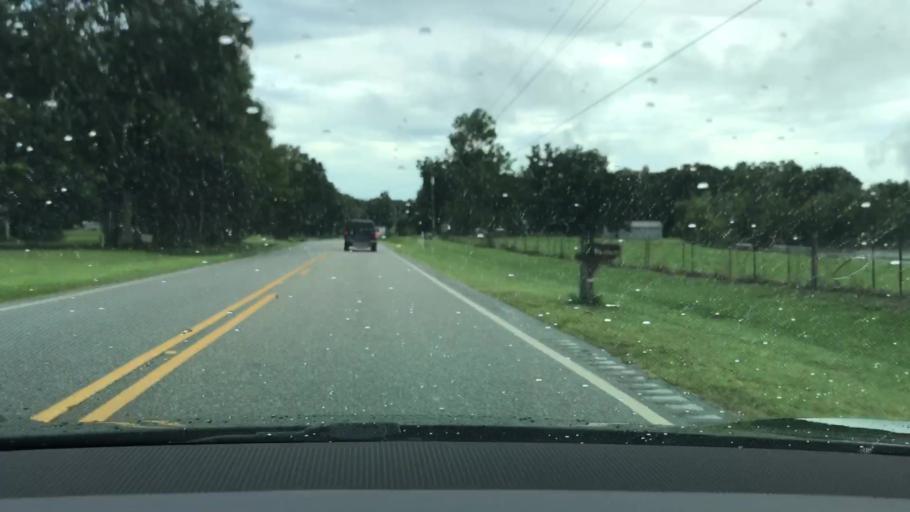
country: US
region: Alabama
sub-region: Geneva County
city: Samson
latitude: 31.0863
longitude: -86.1080
